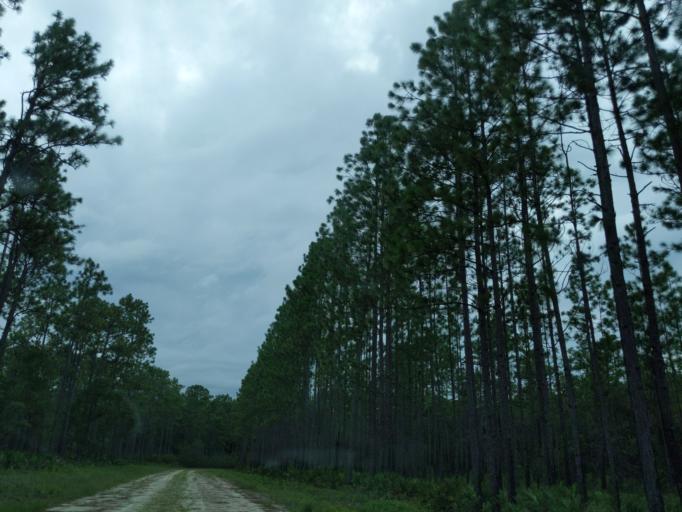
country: US
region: Florida
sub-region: Gadsden County
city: Midway
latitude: 30.3565
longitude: -84.4990
